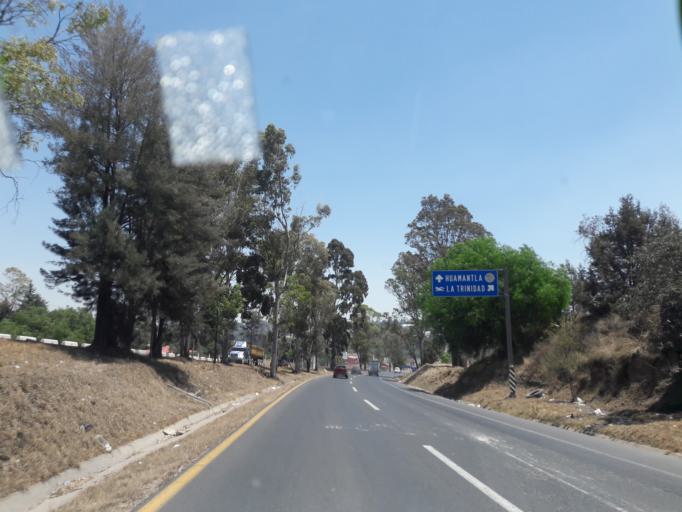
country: MX
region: Tlaxcala
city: Yauhquemehcan
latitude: 19.4058
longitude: -98.1707
